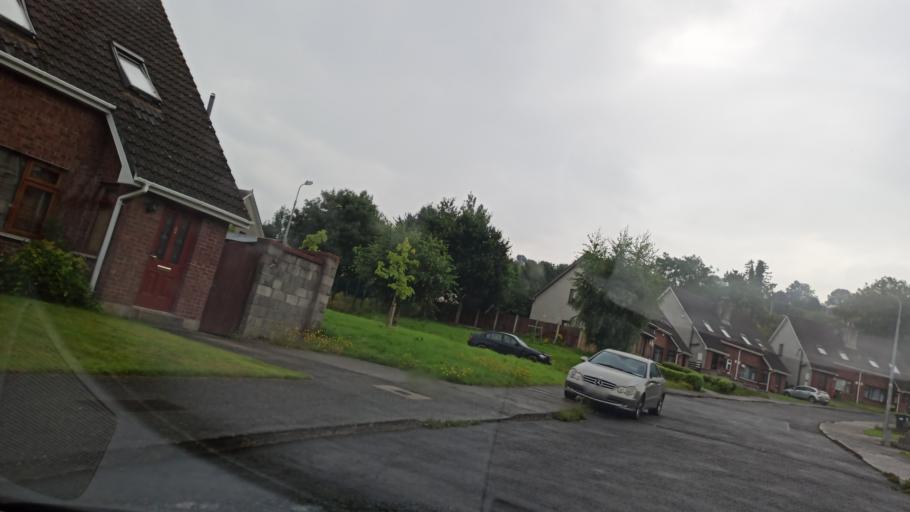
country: IE
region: Munster
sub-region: South Tipperary
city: Cluain Meala
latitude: 52.3467
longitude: -7.7071
